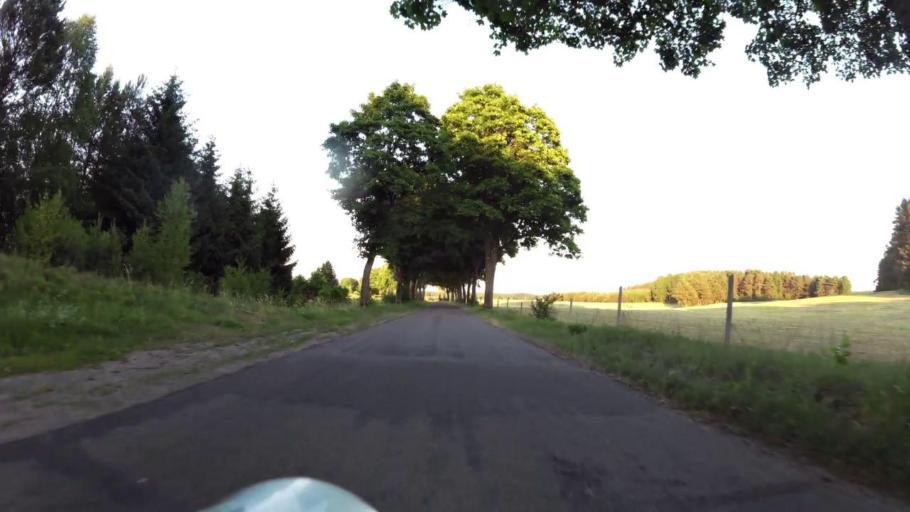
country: PL
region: West Pomeranian Voivodeship
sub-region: Powiat szczecinecki
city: Bialy Bor
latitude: 53.8611
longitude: 16.7258
